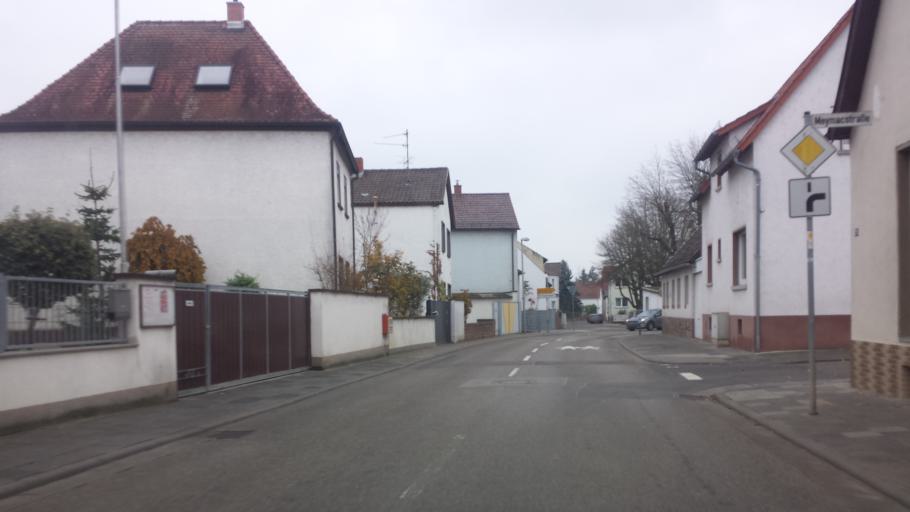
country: DE
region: Hesse
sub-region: Regierungsbezirk Darmstadt
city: Burstadt
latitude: 49.6573
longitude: 8.4096
